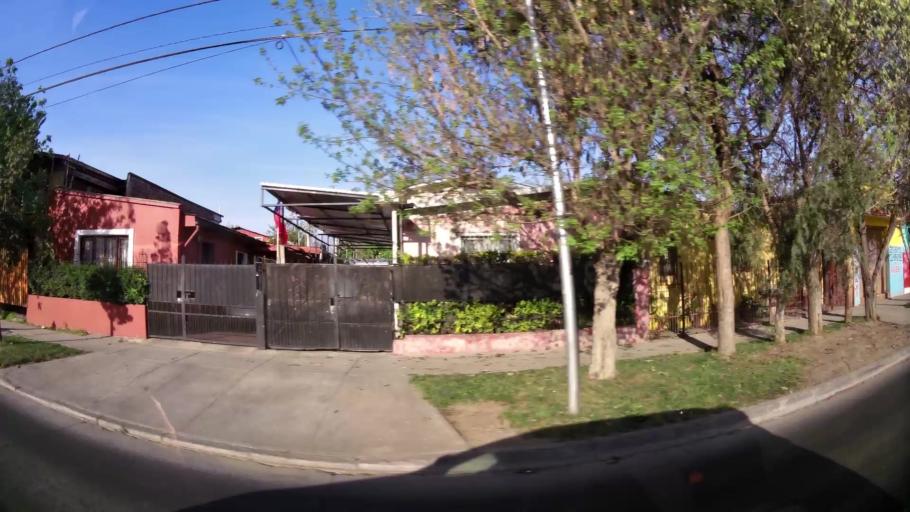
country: CL
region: Santiago Metropolitan
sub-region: Provincia de Santiago
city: Santiago
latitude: -33.5148
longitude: -70.6247
